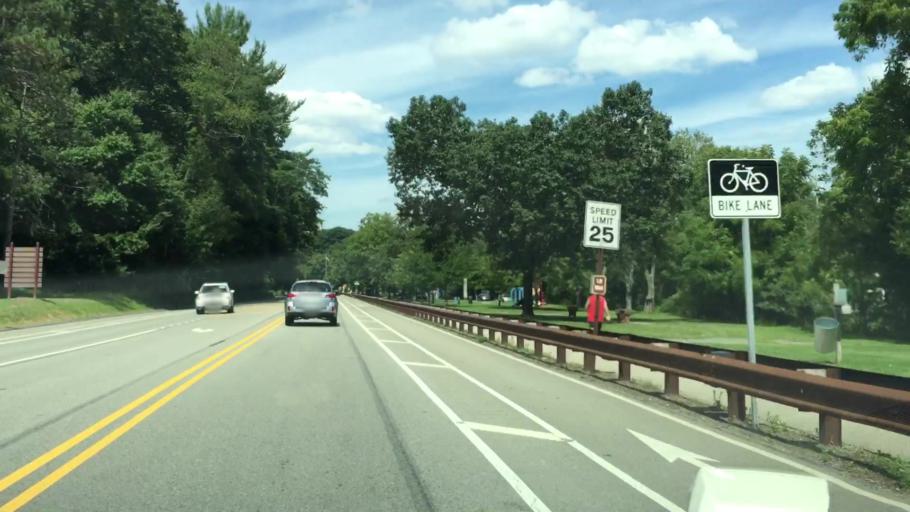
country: US
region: Pennsylvania
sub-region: Allegheny County
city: South Park Township
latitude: 40.3155
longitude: -80.0062
